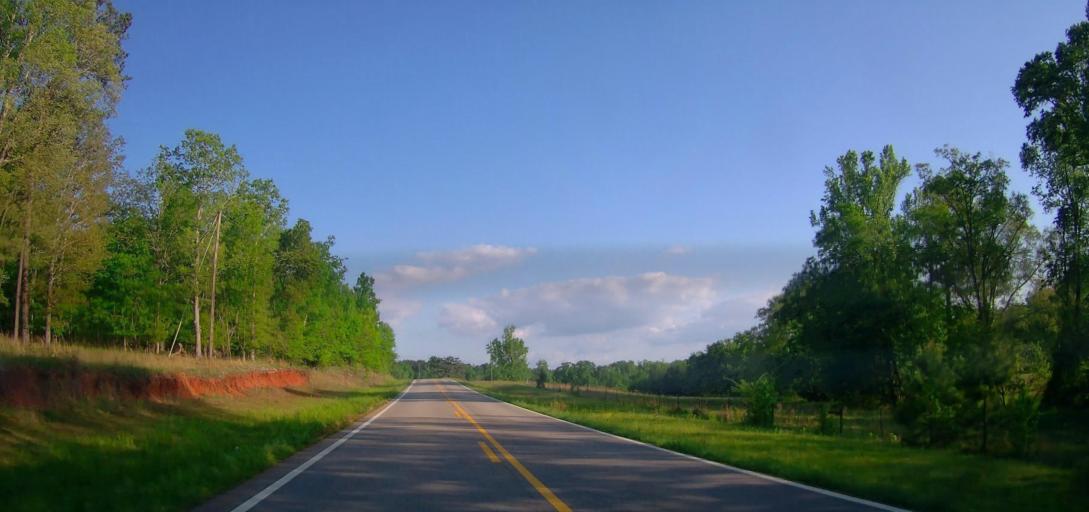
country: US
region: Georgia
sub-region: Putnam County
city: Eatonton
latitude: 33.2923
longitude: -83.3321
